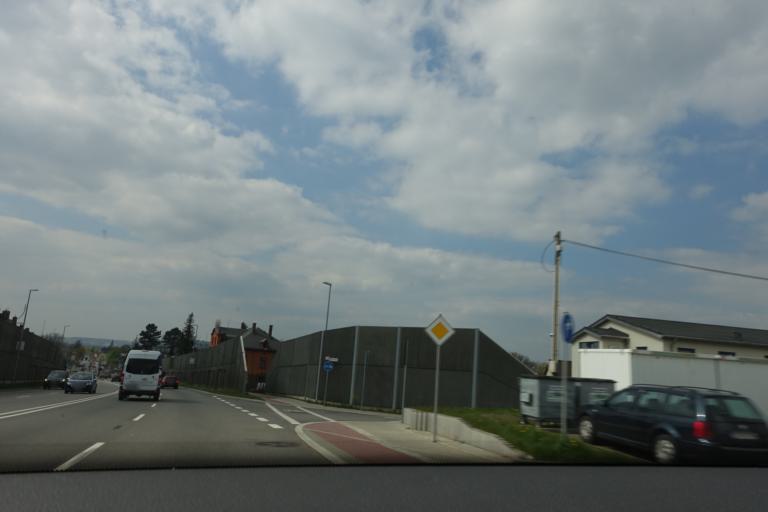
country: DE
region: Saxony
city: Chemnitz
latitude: 50.8102
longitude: 12.9648
